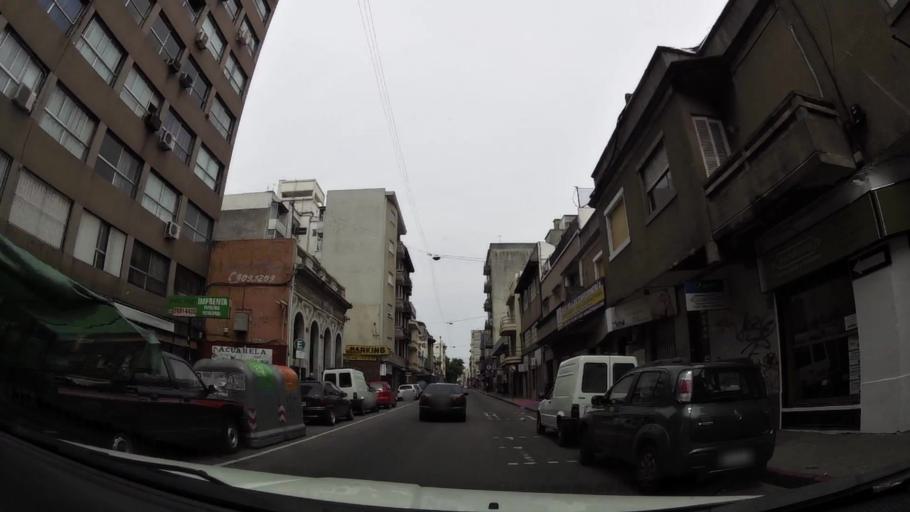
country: UY
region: Montevideo
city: Montevideo
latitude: -34.9016
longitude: -56.1780
